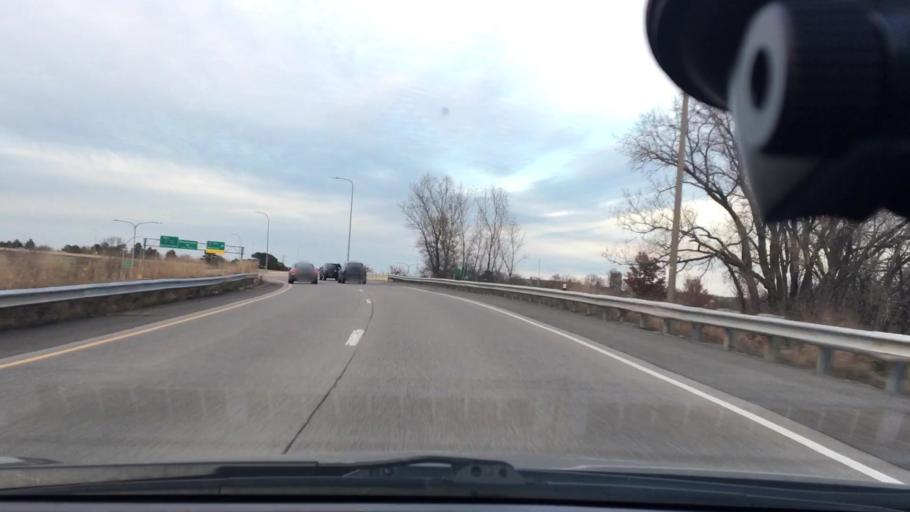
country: US
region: Minnesota
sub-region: Dakota County
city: Mendota Heights
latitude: 44.8885
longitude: -93.1860
